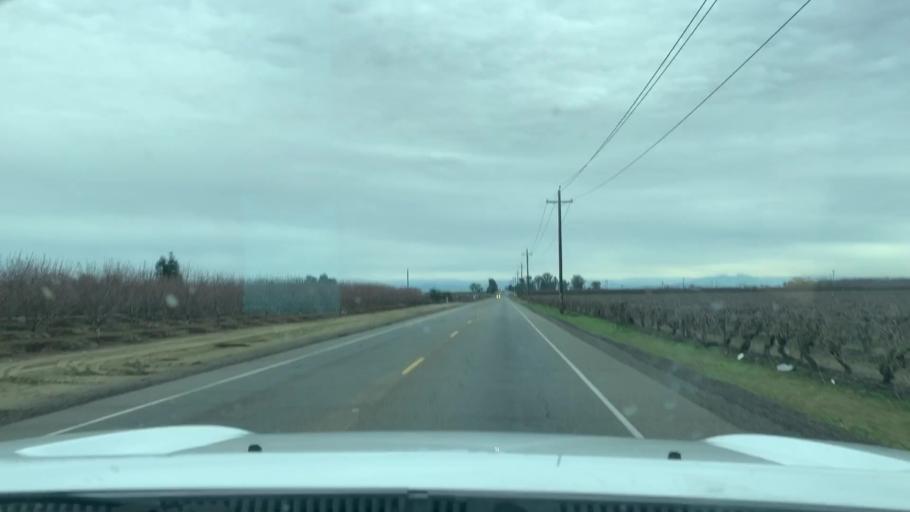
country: US
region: California
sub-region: Fresno County
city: Fowler
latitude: 36.6055
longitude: -119.6754
